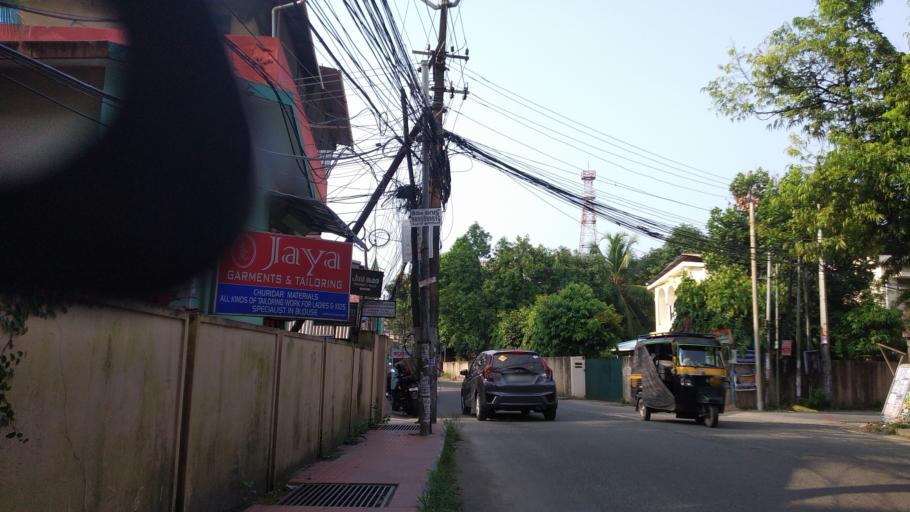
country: IN
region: Kerala
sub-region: Ernakulam
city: Elur
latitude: 10.0000
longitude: 76.2962
